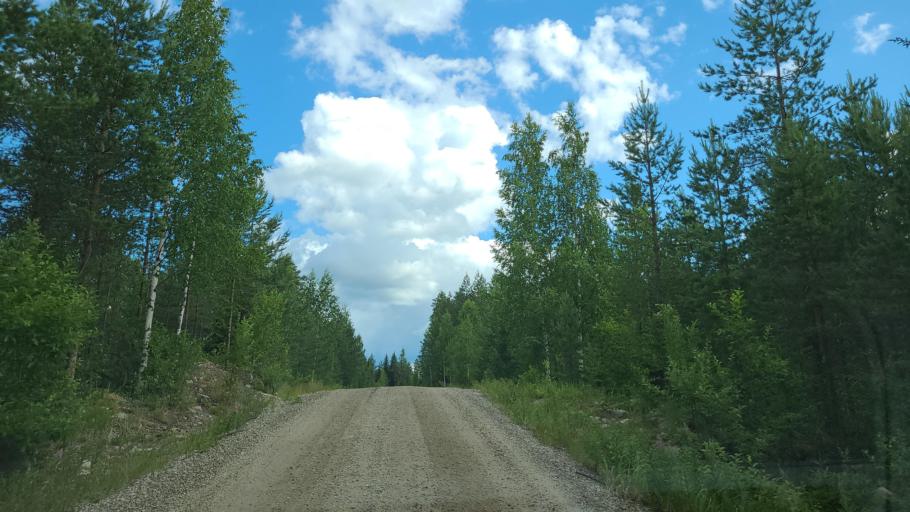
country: FI
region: Northern Savo
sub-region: Koillis-Savo
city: Kaavi
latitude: 63.0382
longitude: 28.8015
